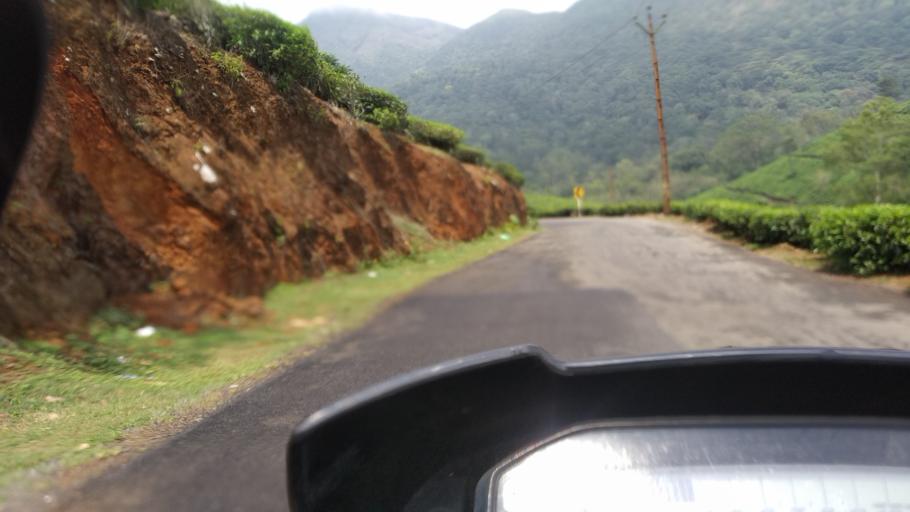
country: IN
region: Kerala
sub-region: Kottayam
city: Erattupetta
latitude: 9.6256
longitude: 76.9703
